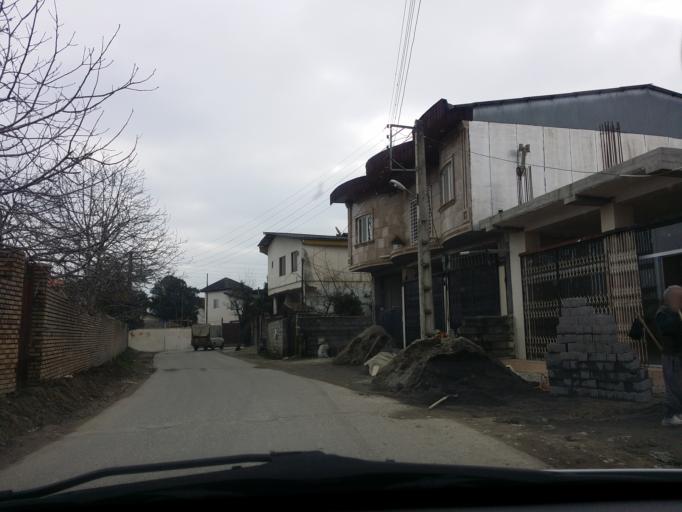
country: IR
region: Mazandaran
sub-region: Nowshahr
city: Nowshahr
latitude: 36.6502
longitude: 51.4777
